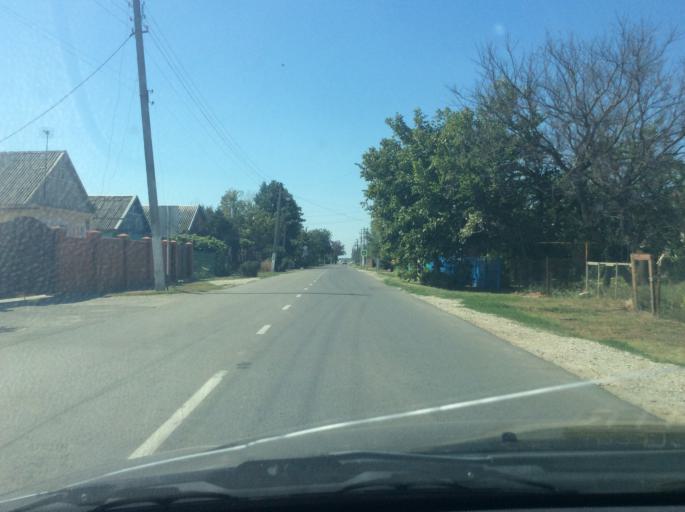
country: RU
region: Krasnodarskiy
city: Slavyansk-na-Kubani
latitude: 45.2497
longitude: 38.1065
